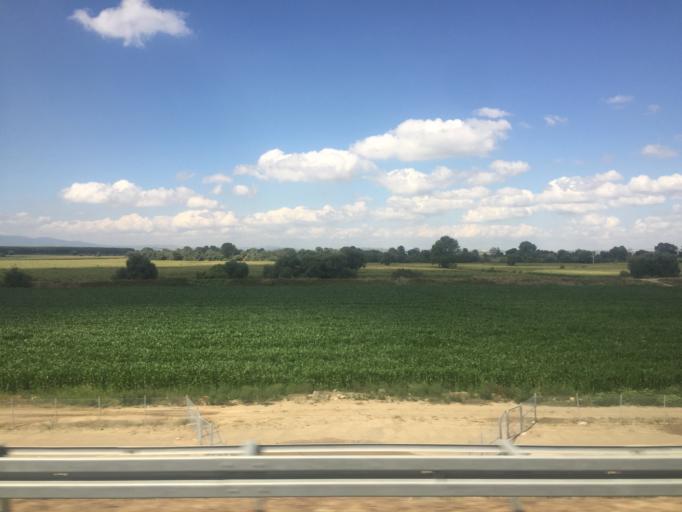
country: TR
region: Bursa
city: Tatkavakli
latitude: 40.1077
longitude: 28.2773
